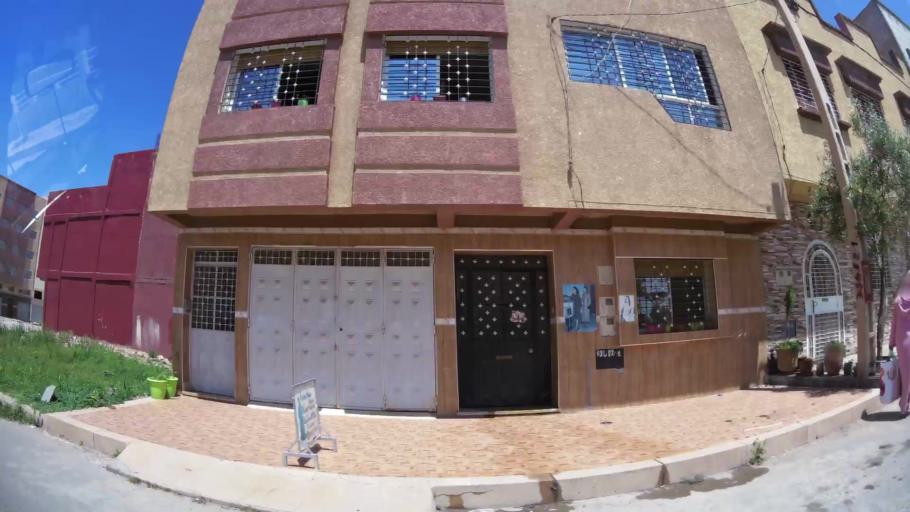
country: MA
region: Oriental
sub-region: Oujda-Angad
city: Oujda
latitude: 34.6980
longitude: -1.8903
